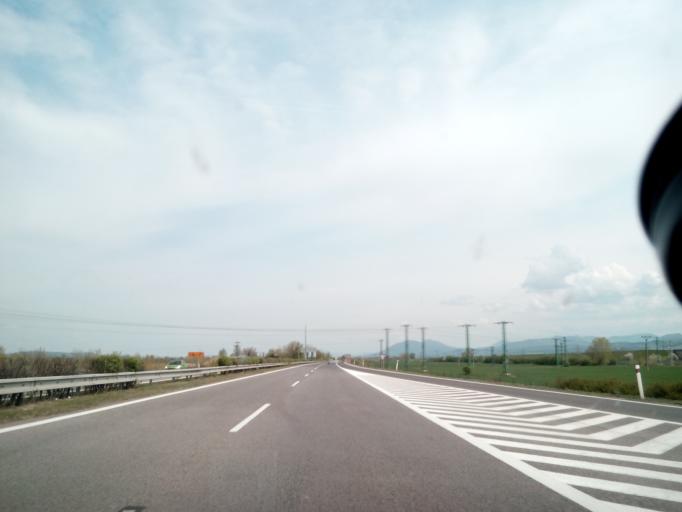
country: SK
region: Nitriansky
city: Nemsova
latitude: 48.9638
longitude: 18.1400
